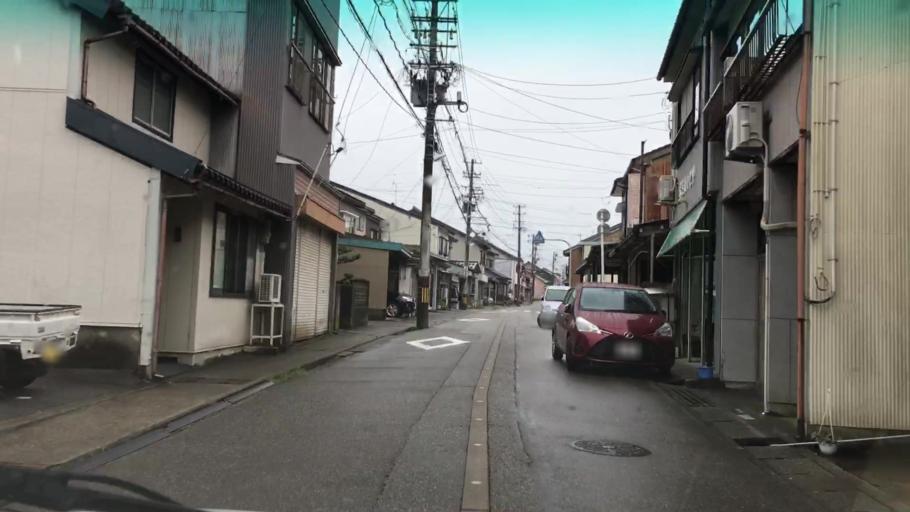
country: JP
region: Toyama
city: Kamiichi
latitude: 36.6618
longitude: 137.3177
